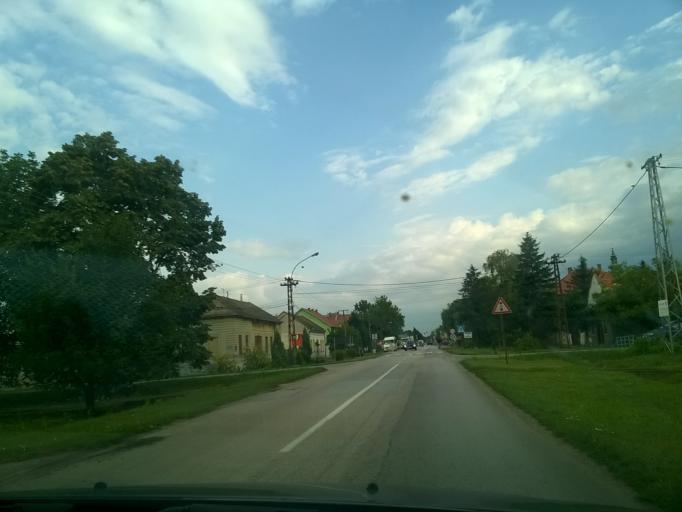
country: RS
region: Autonomna Pokrajina Vojvodina
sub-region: Juznobanatski Okrug
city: Kovacica
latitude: 45.1098
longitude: 20.6190
